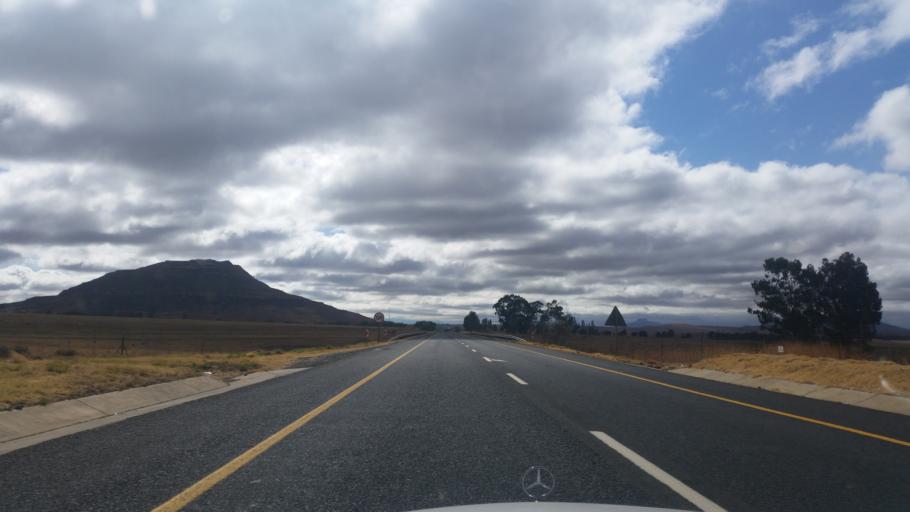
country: ZA
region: Orange Free State
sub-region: Thabo Mofutsanyana District Municipality
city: Phuthaditjhaba
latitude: -28.3131
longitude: 28.7305
